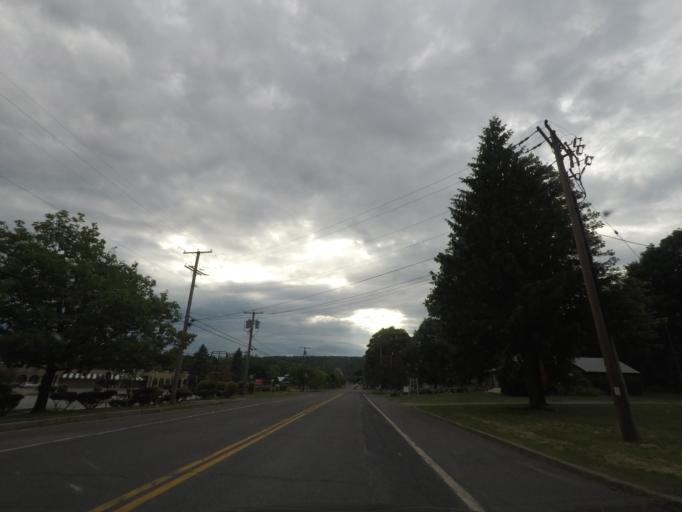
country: US
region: New York
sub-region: Dutchess County
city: Pine Plains
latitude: 41.9525
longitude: -73.5012
